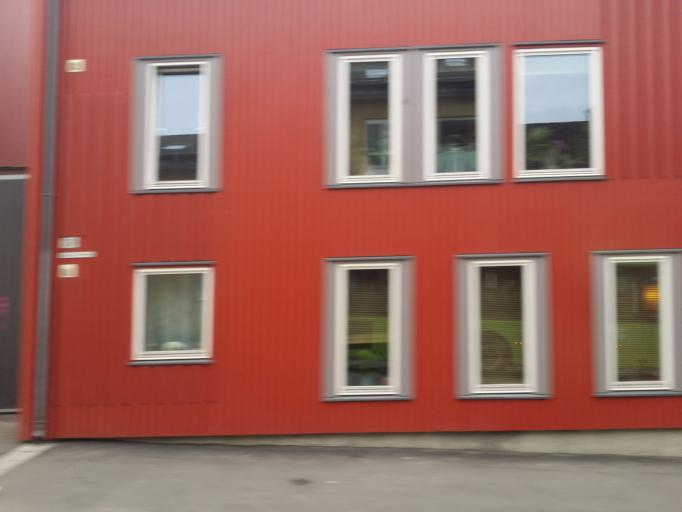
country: NO
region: Oslo
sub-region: Oslo
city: Oslo
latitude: 59.9097
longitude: 10.7897
